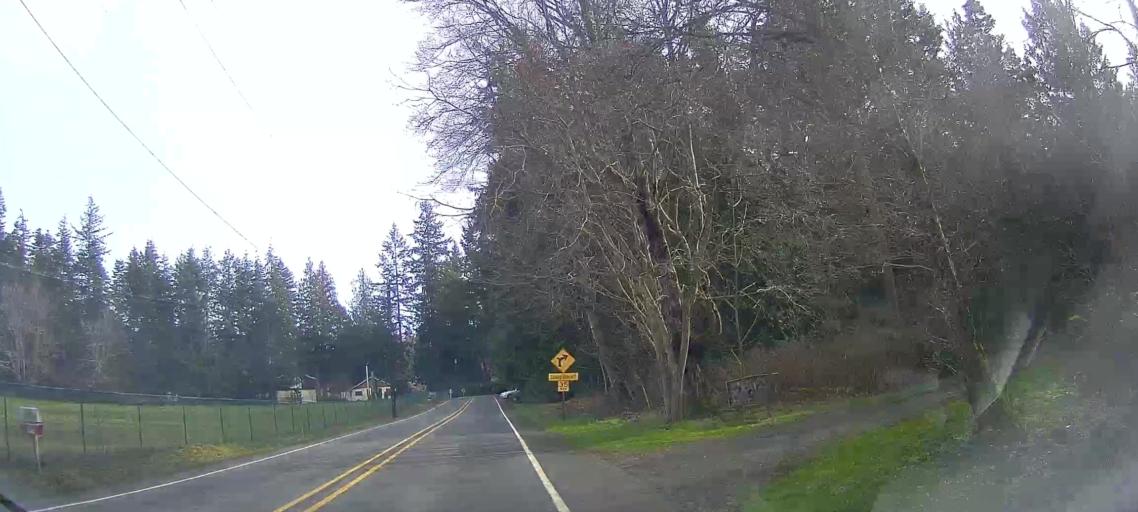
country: US
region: Washington
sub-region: Island County
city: Langley
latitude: 48.1051
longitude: -122.4213
